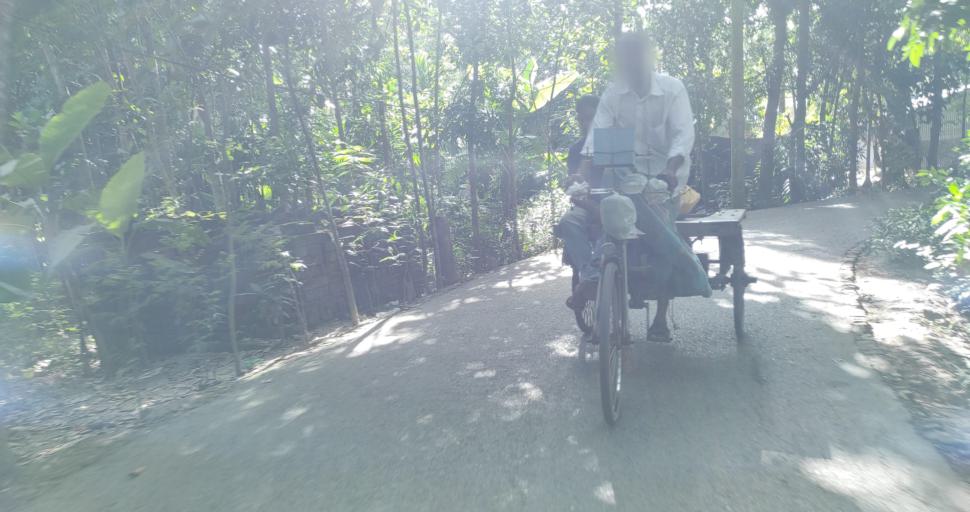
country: BD
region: Barisal
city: Gaurnadi
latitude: 22.8930
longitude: 90.1918
